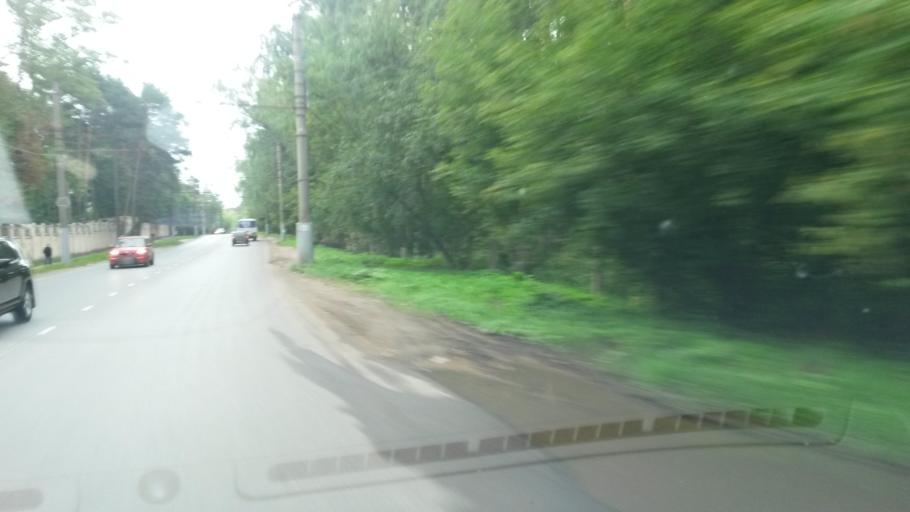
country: RU
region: Ivanovo
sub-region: Gorod Ivanovo
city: Ivanovo
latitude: 57.0255
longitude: 40.9397
